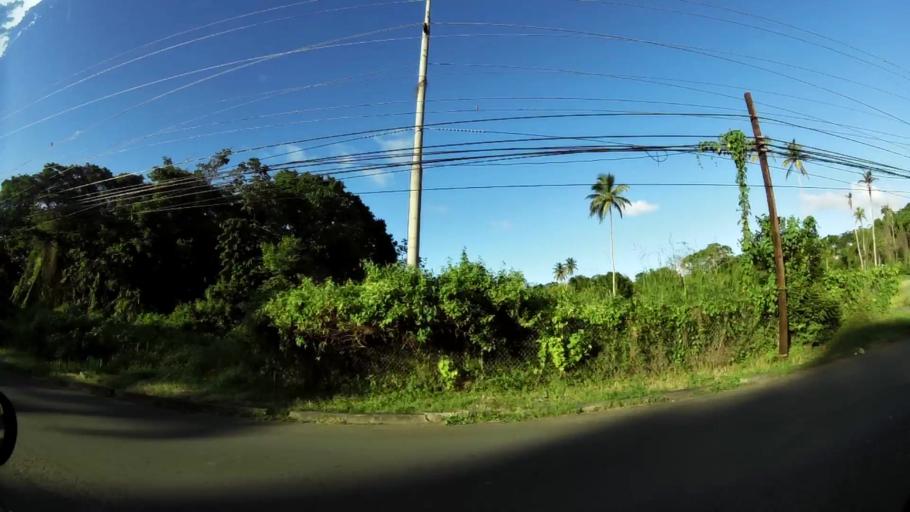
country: TT
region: Tobago
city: Scarborough
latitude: 11.2149
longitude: -60.7692
